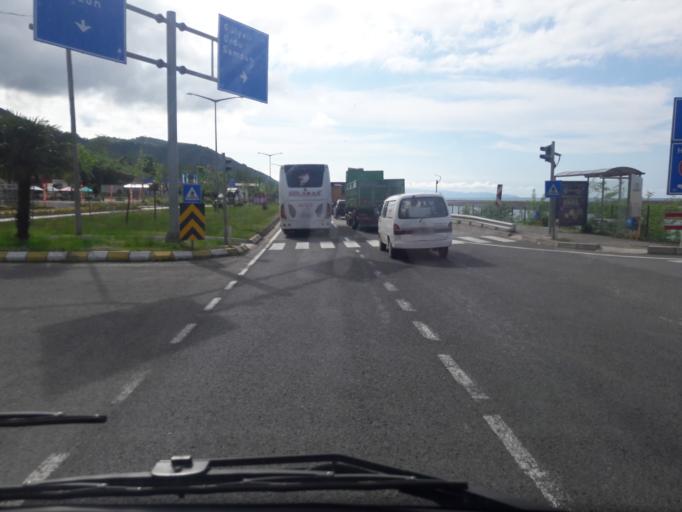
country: TR
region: Ordu
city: Gulyali
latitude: 40.9646
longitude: 38.0743
